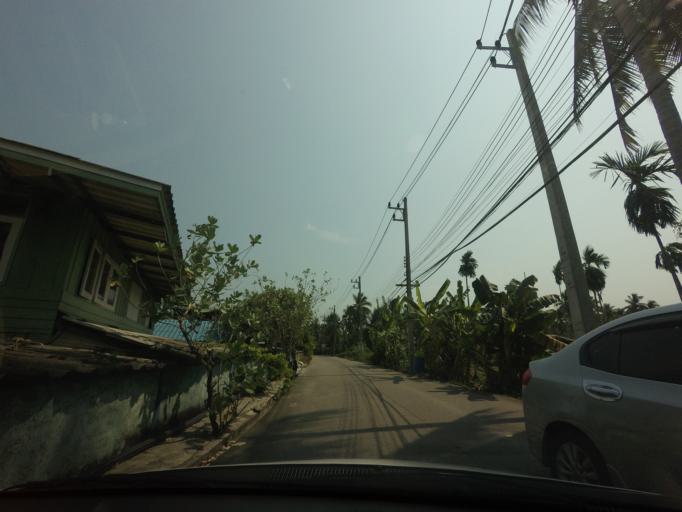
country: TH
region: Nakhon Pathom
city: Sam Phran
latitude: 13.7651
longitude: 100.2591
